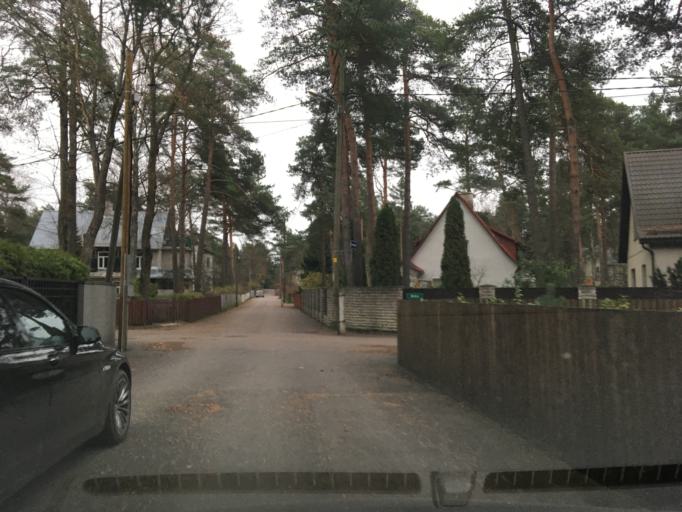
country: EE
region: Harju
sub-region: Saue vald
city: Laagri
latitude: 59.3819
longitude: 24.6859
